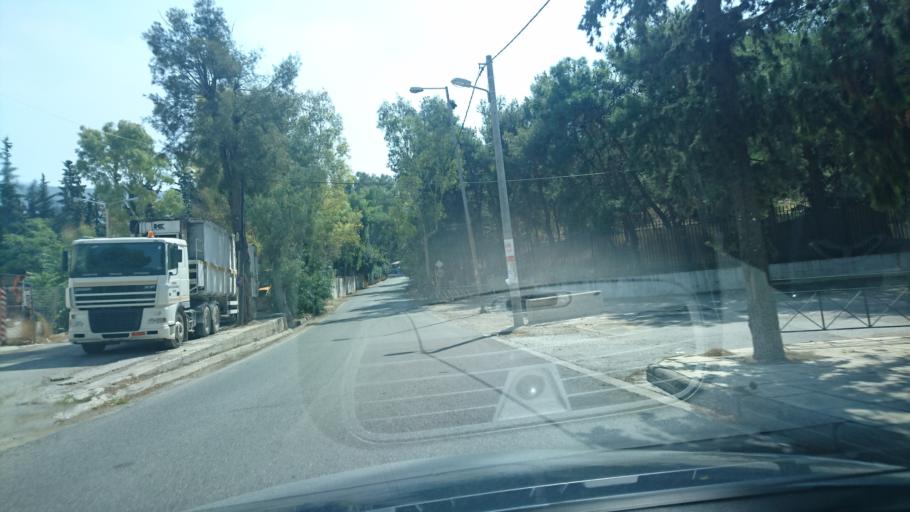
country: GR
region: Attica
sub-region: Nomarchia Athinas
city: Kaisariani
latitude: 37.9648
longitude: 23.7761
